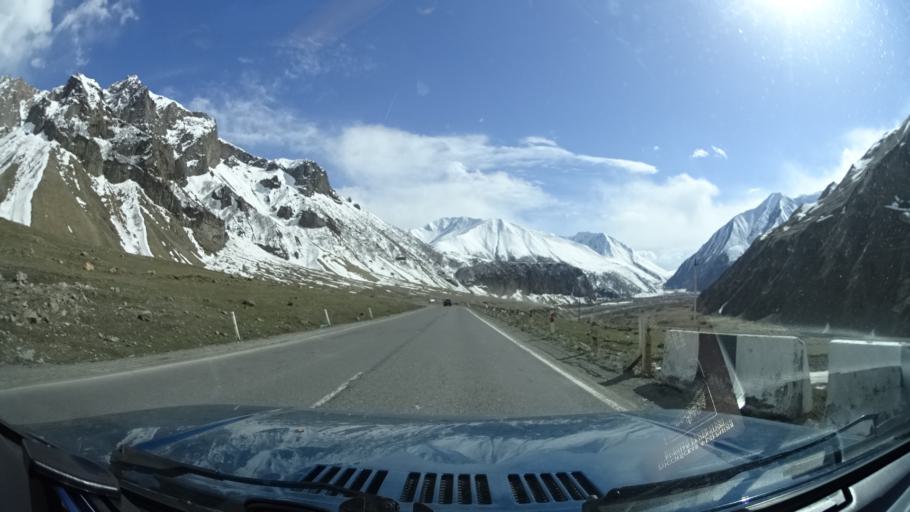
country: GE
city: Gudauri
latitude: 42.5776
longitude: 44.5251
